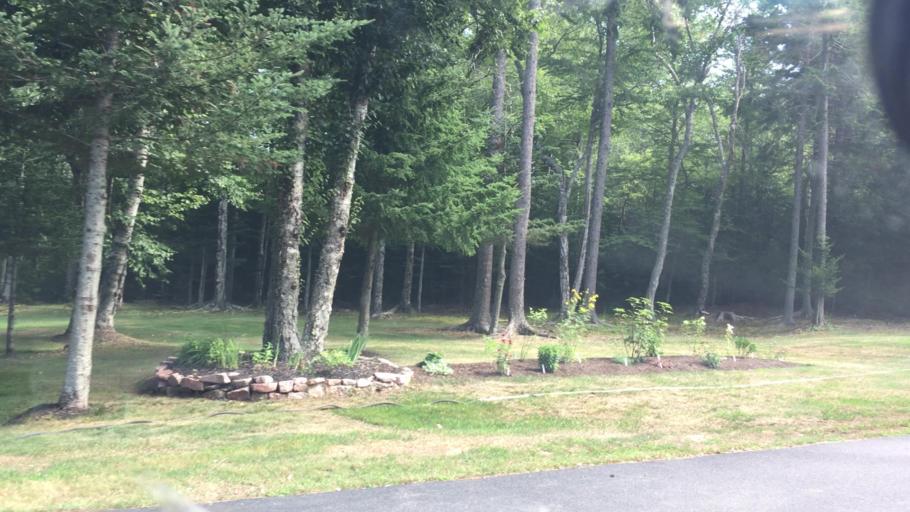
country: US
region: Maine
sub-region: Washington County
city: Eastport
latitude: 44.9346
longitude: -67.0460
